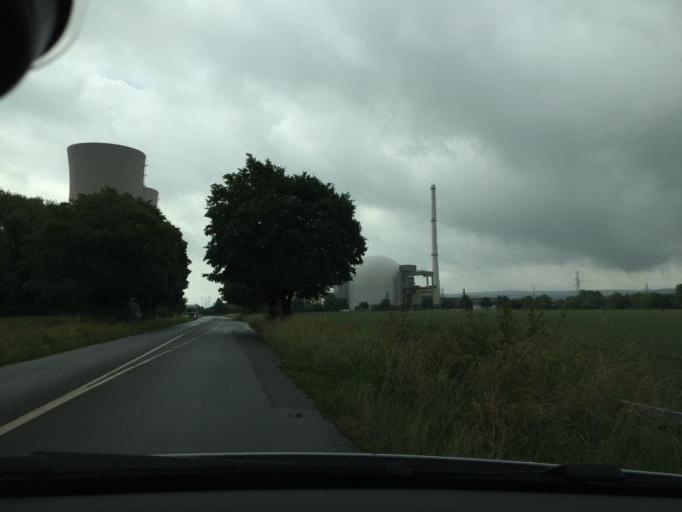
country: DE
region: Lower Saxony
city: Hehlen
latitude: 52.0400
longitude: 9.4074
